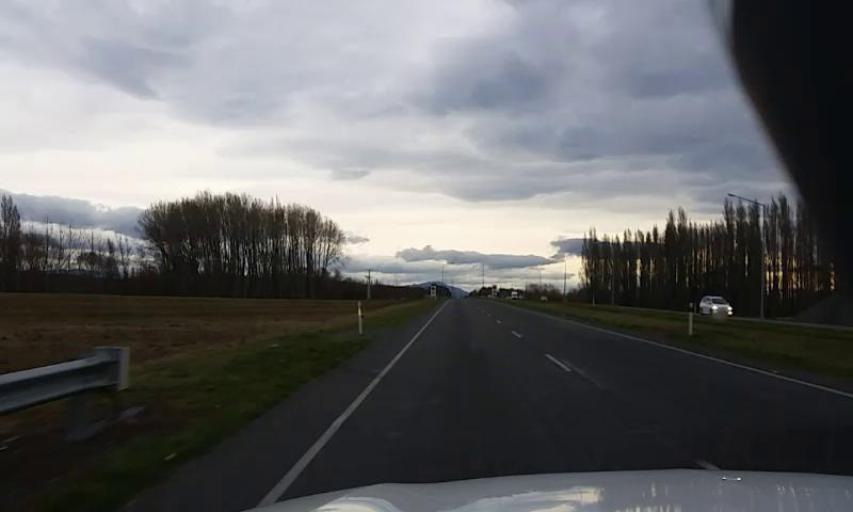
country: NZ
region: Canterbury
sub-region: Waimakariri District
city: Kaiapoi
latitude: -43.4197
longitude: 172.6479
